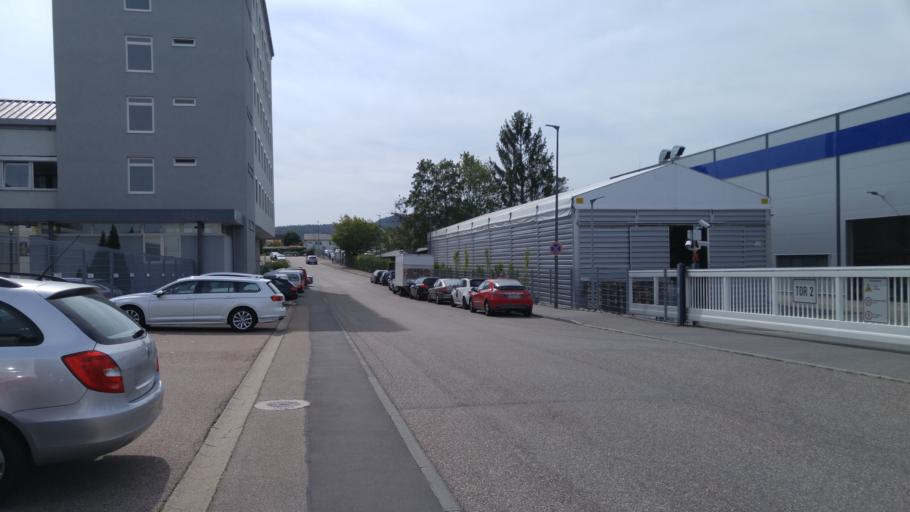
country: DE
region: Baden-Wuerttemberg
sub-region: Regierungsbezirk Stuttgart
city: Leonberg
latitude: 48.7955
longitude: 9.0009
